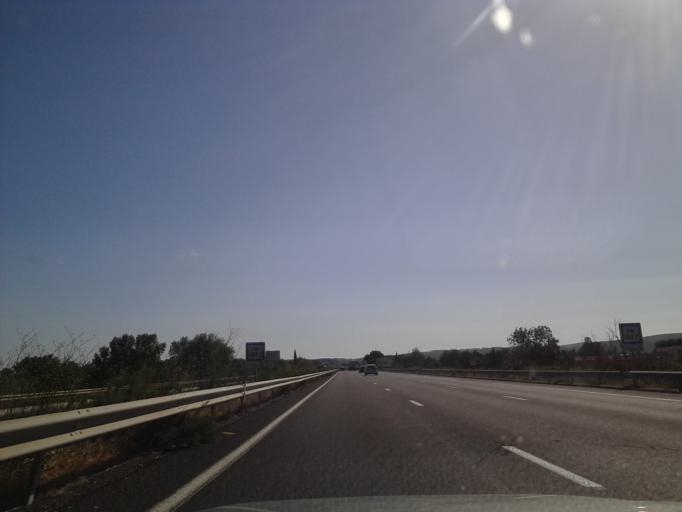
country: FR
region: Languedoc-Roussillon
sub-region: Departement de l'Aude
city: Narbonne
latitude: 43.1707
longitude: 3.0157
